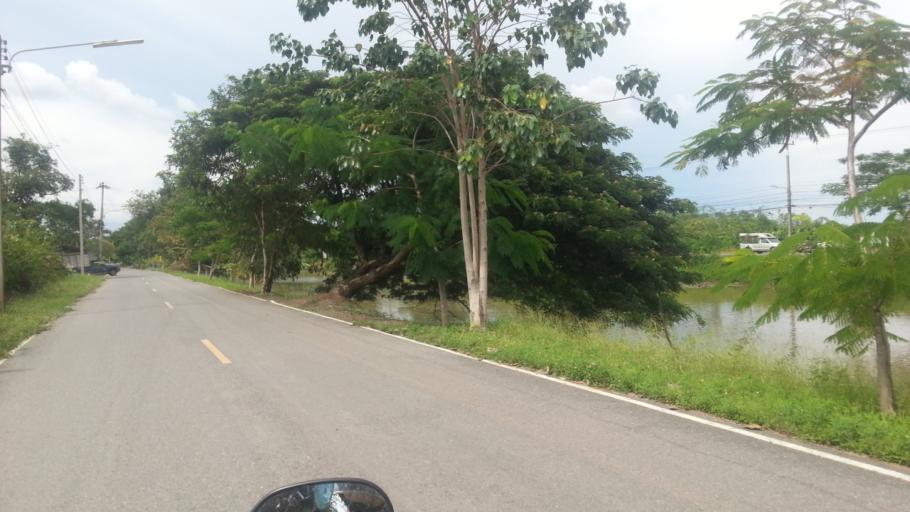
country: TH
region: Pathum Thani
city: Nong Suea
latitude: 14.0939
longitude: 100.8237
